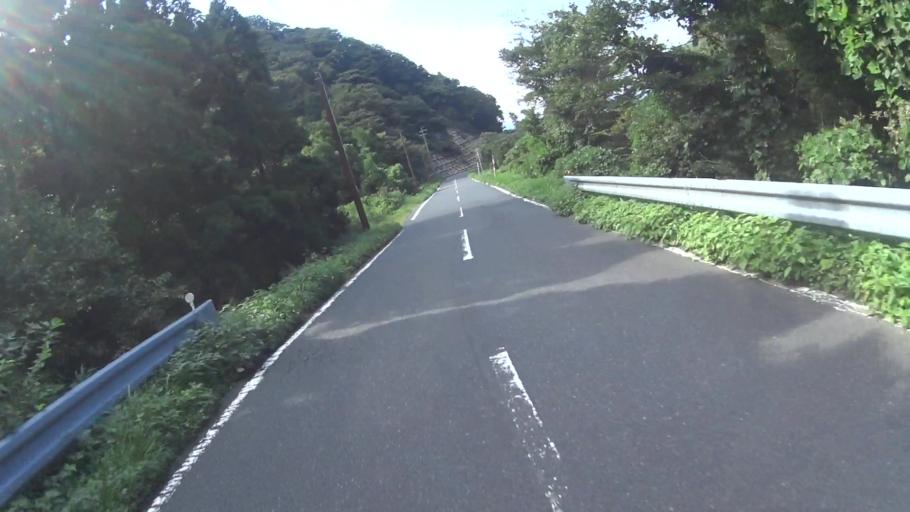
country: JP
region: Kyoto
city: Miyazu
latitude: 35.7677
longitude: 135.2263
